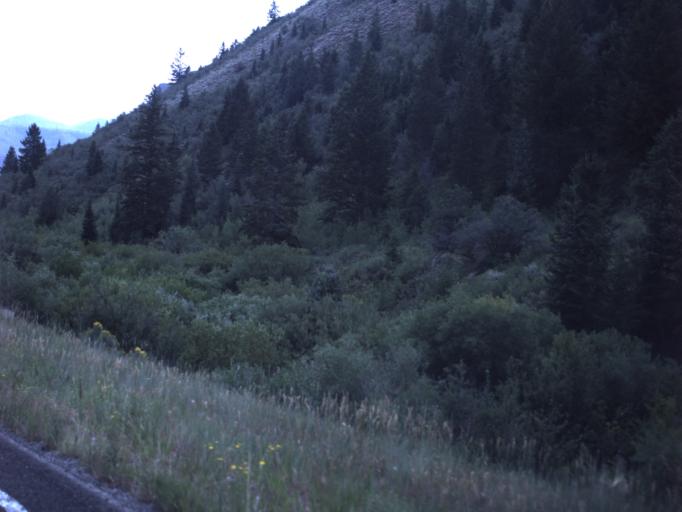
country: US
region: Utah
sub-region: Summit County
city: Francis
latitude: 40.4711
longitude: -110.9064
